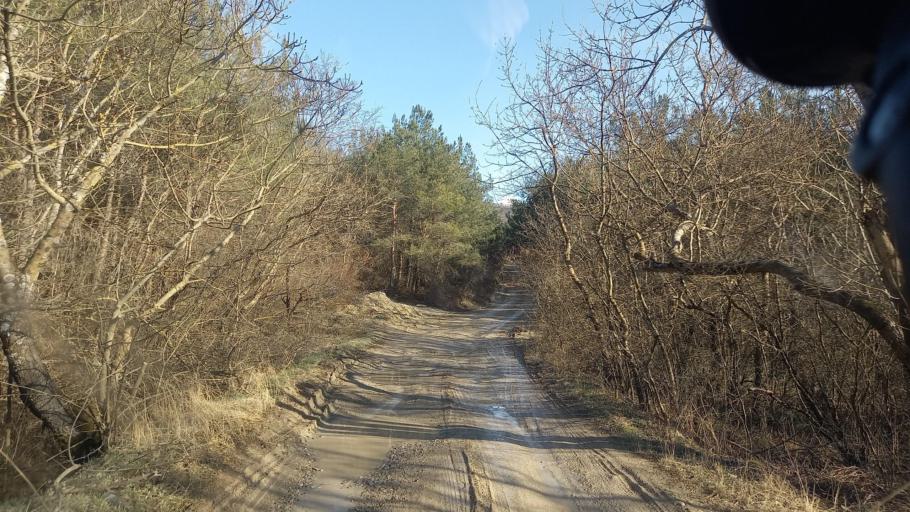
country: RU
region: Krasnodarskiy
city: Kabardinka
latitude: 44.6296
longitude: 37.9270
